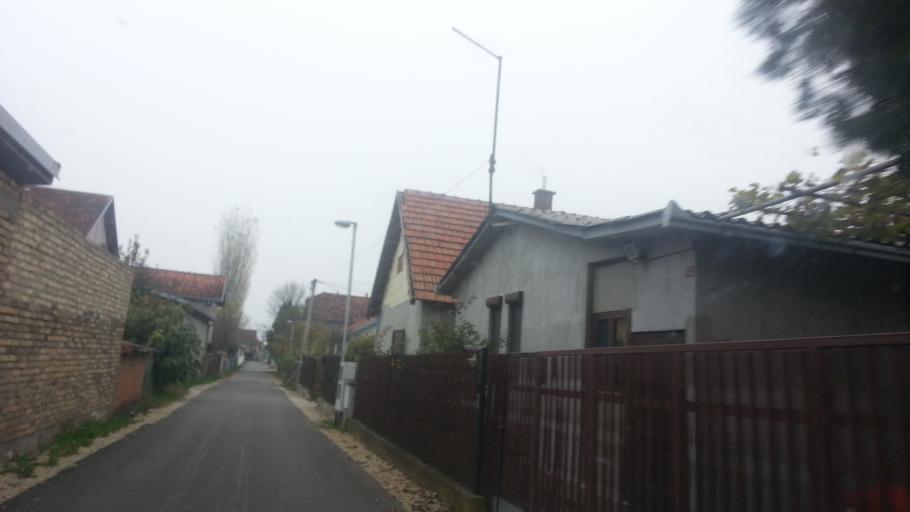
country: RS
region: Autonomna Pokrajina Vojvodina
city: Nova Pazova
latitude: 44.9561
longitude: 20.2180
